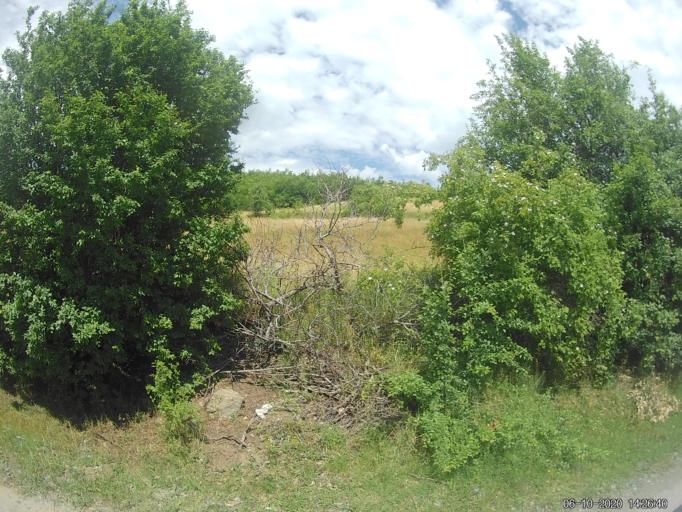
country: XK
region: Prizren
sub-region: Komuna e Therandes
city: Budakovo
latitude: 42.4093
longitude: 20.9157
